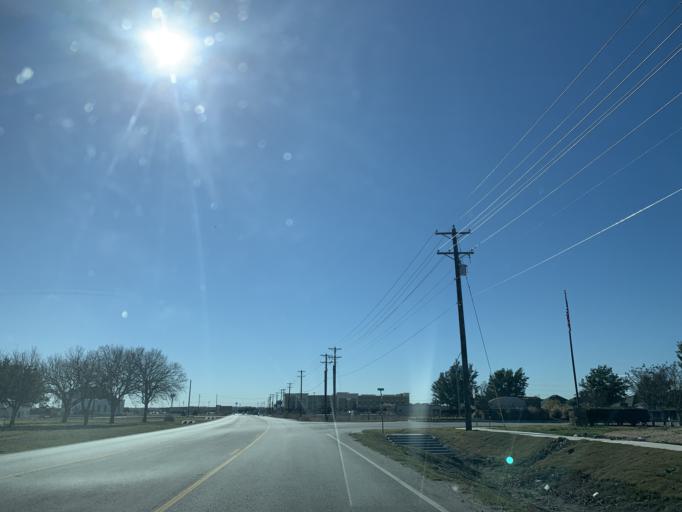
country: US
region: Texas
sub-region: Williamson County
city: Hutto
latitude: 30.5480
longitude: -97.5609
